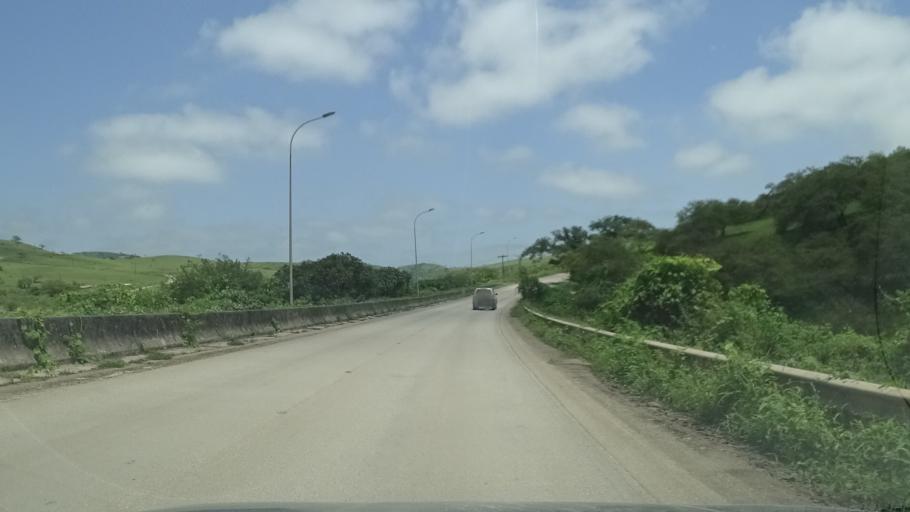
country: OM
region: Zufar
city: Salalah
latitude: 17.1875
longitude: 54.2443
